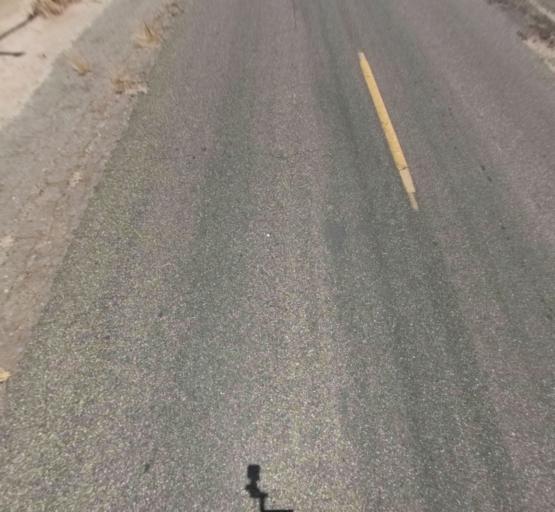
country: US
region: California
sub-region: Madera County
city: Parkwood
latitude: 36.8686
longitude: -120.0922
